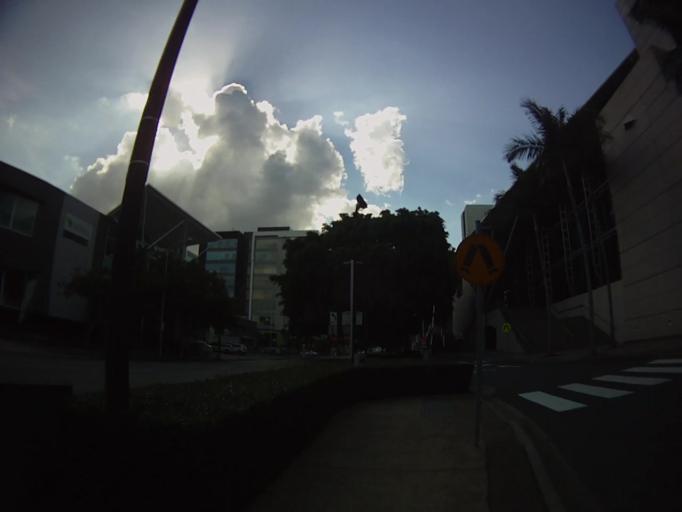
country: AU
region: Queensland
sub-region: Brisbane
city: South Brisbane
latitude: -27.4774
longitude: 153.0183
